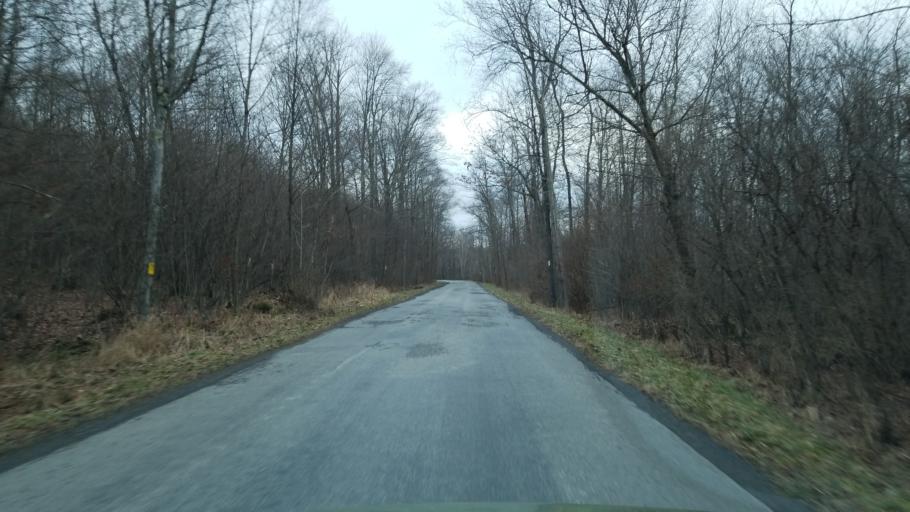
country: US
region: Pennsylvania
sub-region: Jefferson County
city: Falls Creek
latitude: 41.1775
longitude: -78.7933
